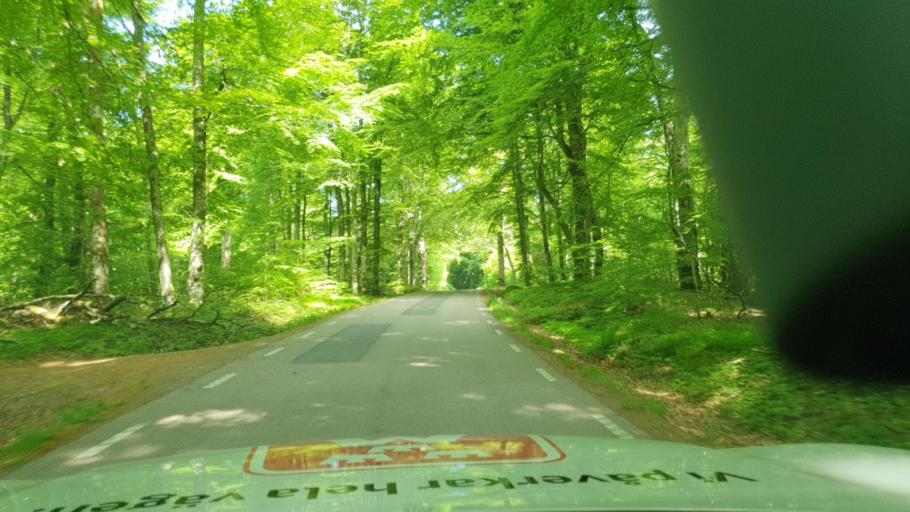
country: SE
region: Vaestra Goetaland
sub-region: Herrljunga Kommun
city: Herrljunga
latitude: 57.9231
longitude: 13.1293
